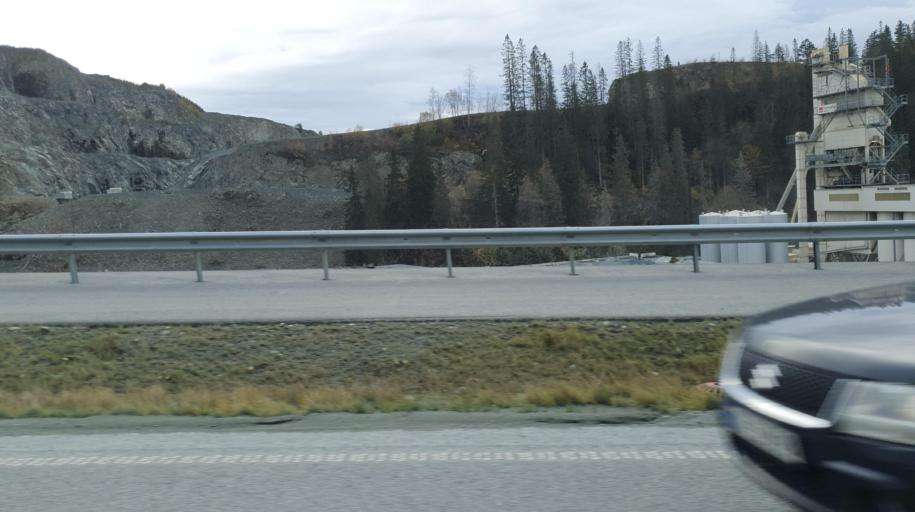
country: NO
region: Sor-Trondelag
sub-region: Klaebu
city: Klaebu
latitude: 63.3194
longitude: 10.3848
